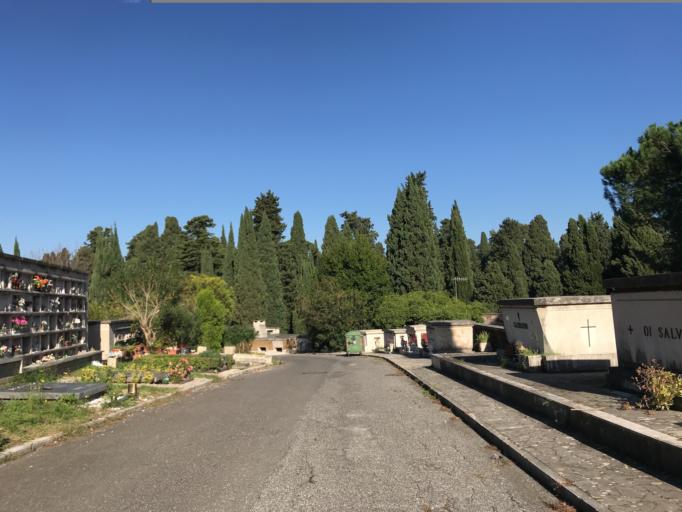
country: IT
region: Latium
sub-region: Citta metropolitana di Roma Capitale
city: Rome
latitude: 41.9006
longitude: 12.5235
